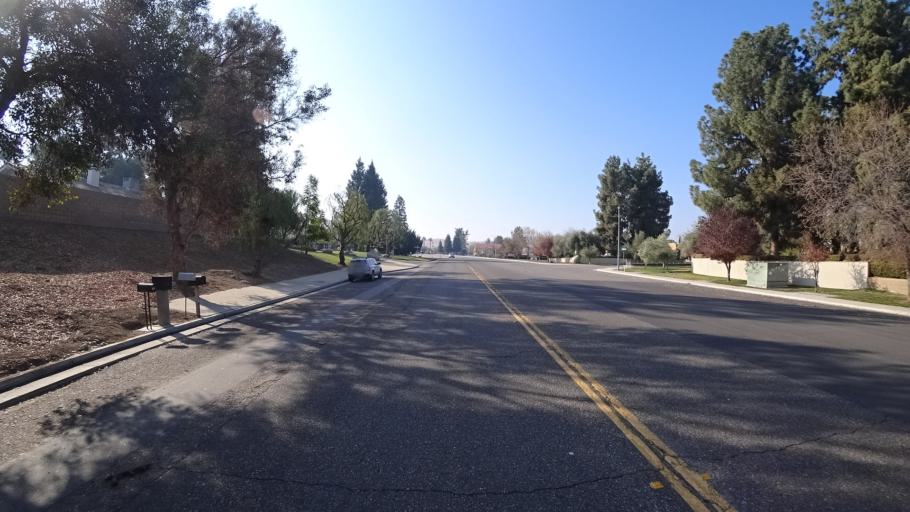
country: US
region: California
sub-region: Kern County
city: Oildale
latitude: 35.4317
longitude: -118.8677
